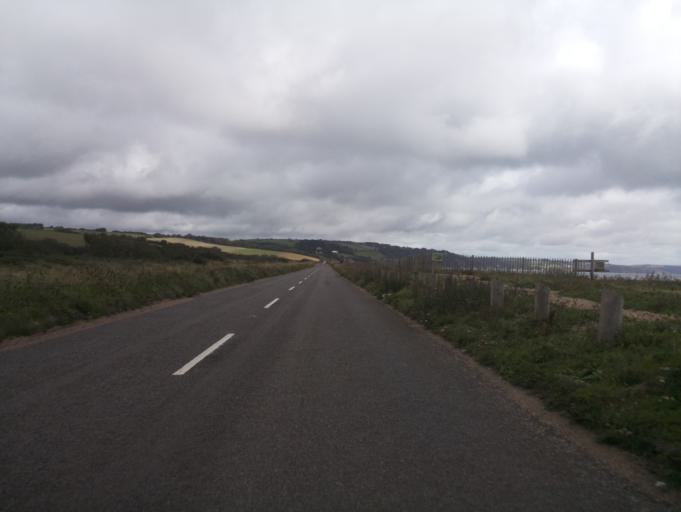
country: GB
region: England
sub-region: Devon
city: Dartmouth
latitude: 50.2817
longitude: -3.6477
